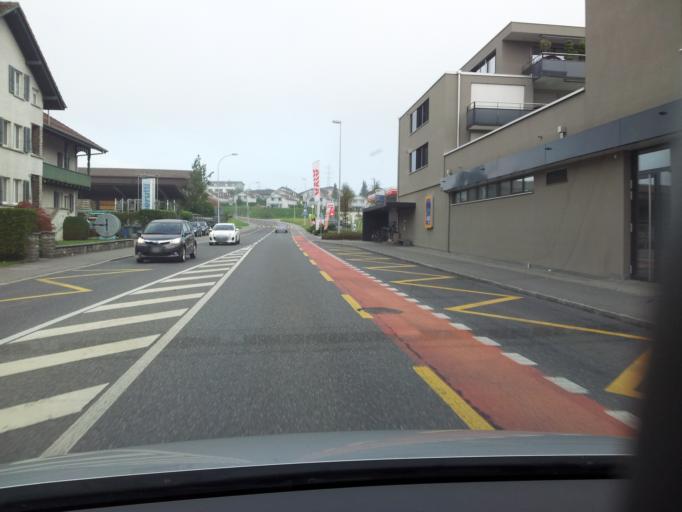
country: CH
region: Lucerne
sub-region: Hochdorf District
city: Emmen
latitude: 47.1003
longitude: 8.2680
